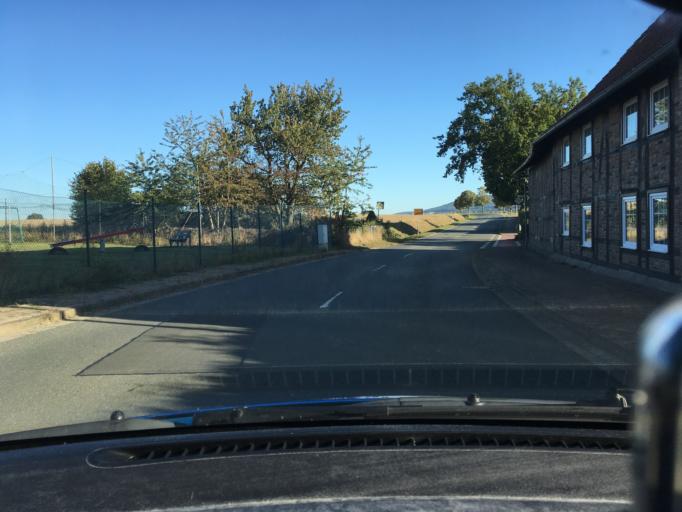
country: DE
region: Lower Saxony
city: Hulsede
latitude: 52.2445
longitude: 9.3739
